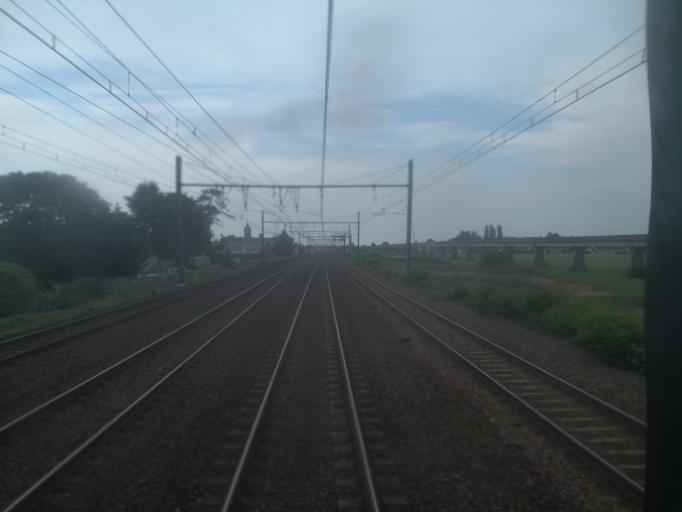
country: FR
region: Centre
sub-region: Departement du Loiret
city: Saran
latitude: 47.9830
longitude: 1.8852
